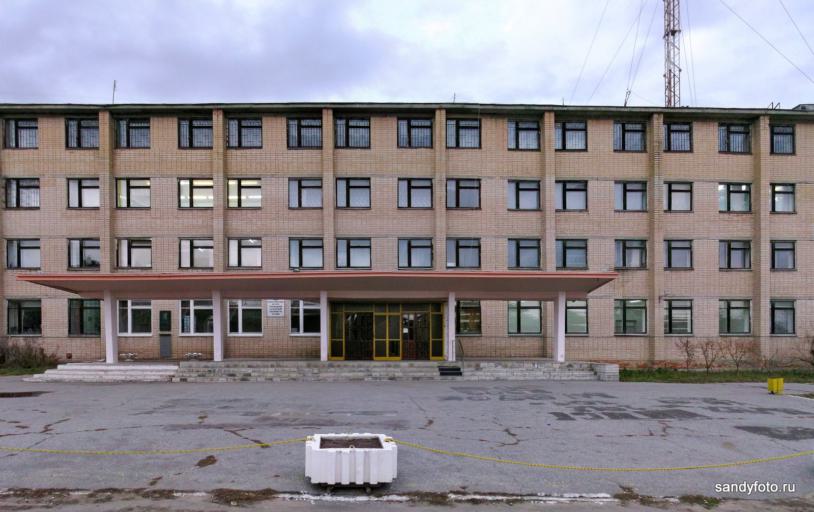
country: RU
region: Chelyabinsk
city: Troitsk
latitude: 54.0810
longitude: 61.5621
